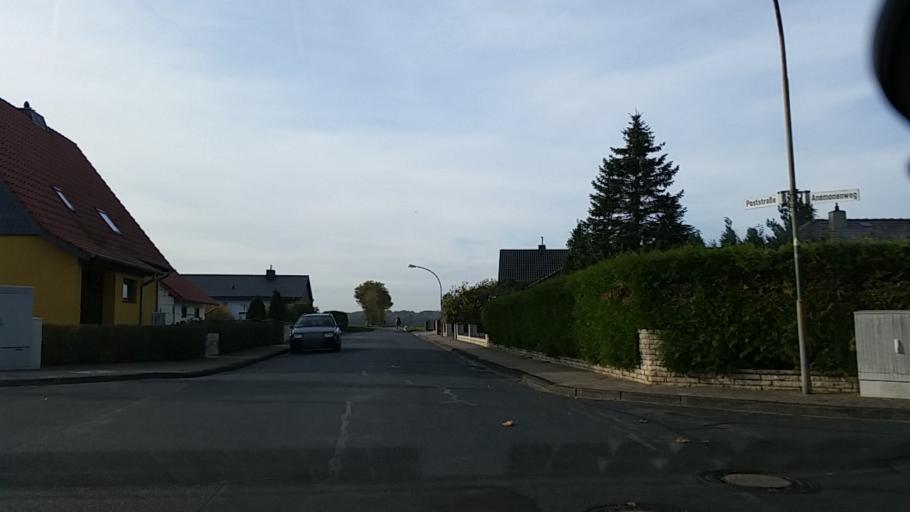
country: DE
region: Lower Saxony
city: Tappenbeck
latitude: 52.4715
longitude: 10.7370
